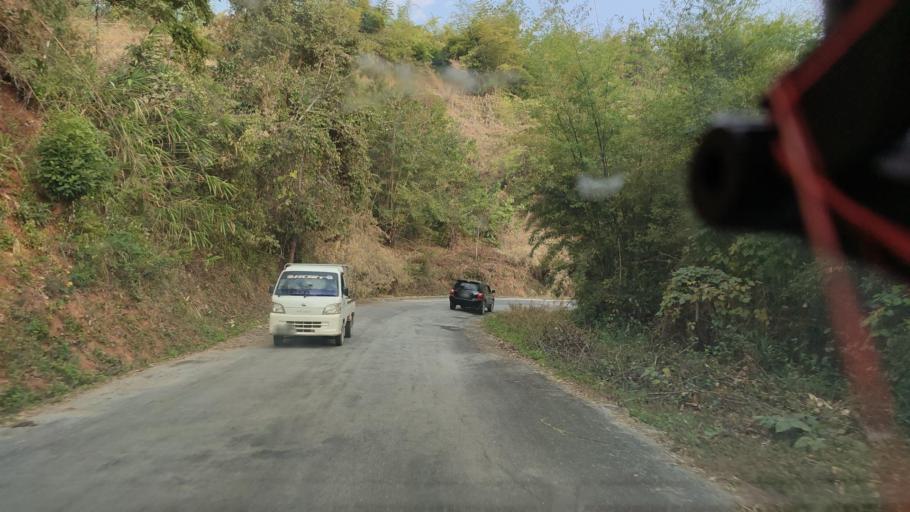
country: CN
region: Yunnan
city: Nayun
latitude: 21.4389
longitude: 99.6287
